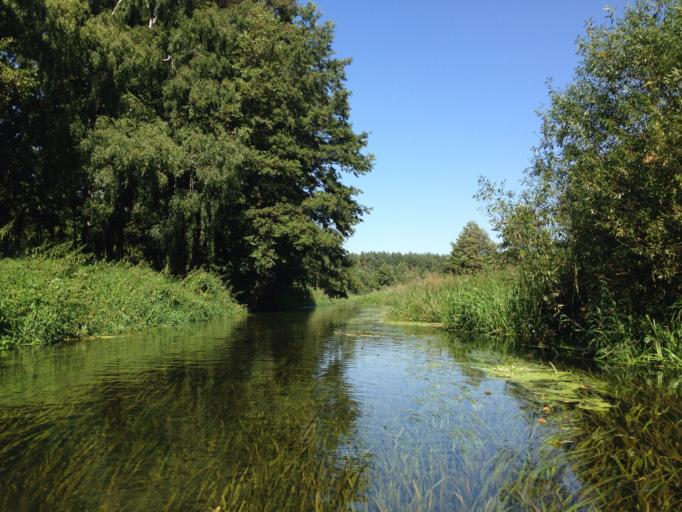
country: PL
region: Kujawsko-Pomorskie
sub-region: Powiat brodnicki
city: Bartniczka
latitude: 53.2780
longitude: 19.5853
